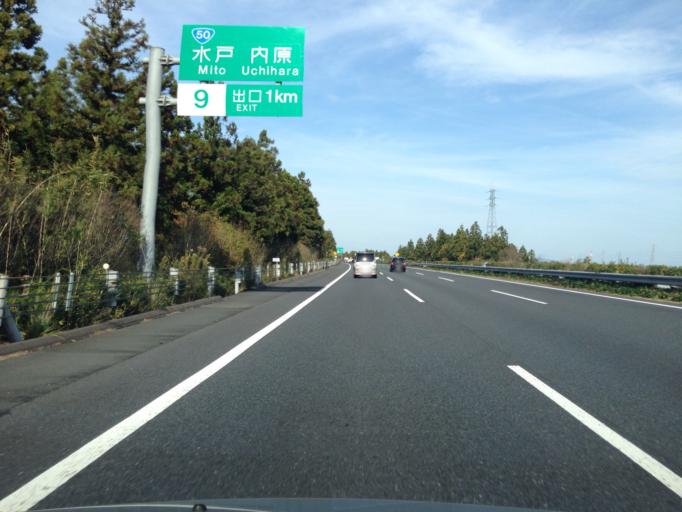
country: JP
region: Ibaraki
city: Mito-shi
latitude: 36.3719
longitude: 140.3835
